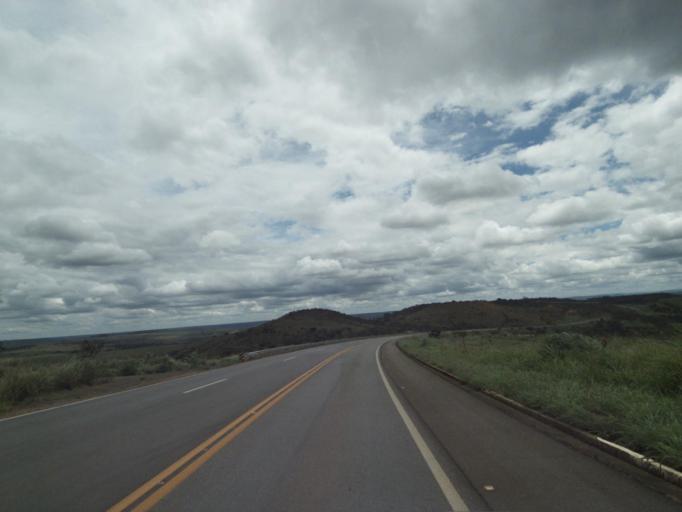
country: BR
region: Federal District
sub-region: Brasilia
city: Brasilia
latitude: -15.7527
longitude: -48.4141
